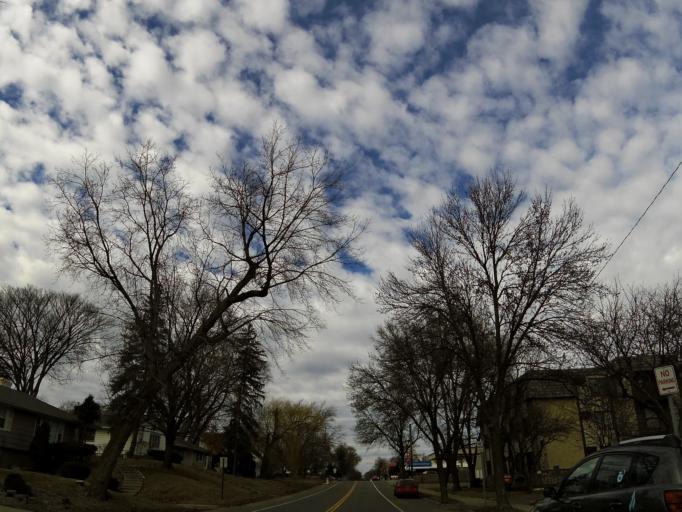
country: US
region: Minnesota
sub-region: Hennepin County
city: Edina
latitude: 44.9002
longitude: -93.3189
